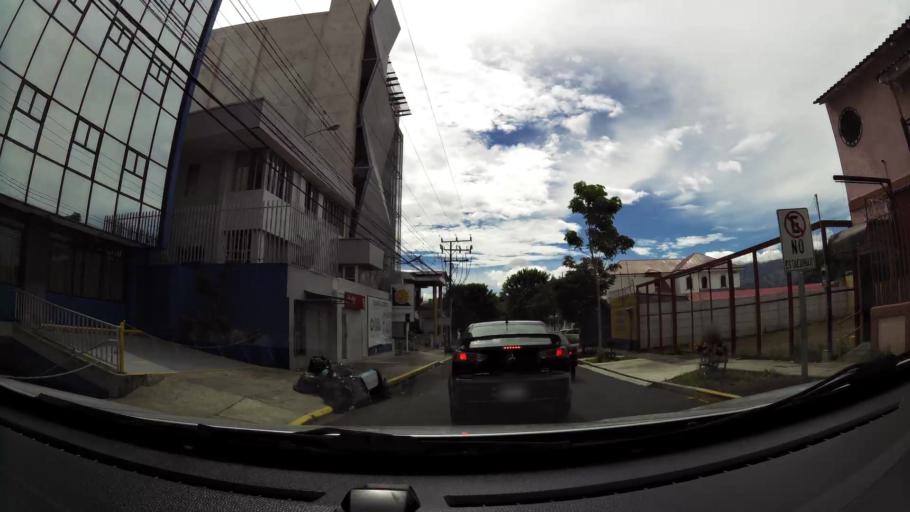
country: CR
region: San Jose
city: San Jose
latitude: 9.9299
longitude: -84.0694
